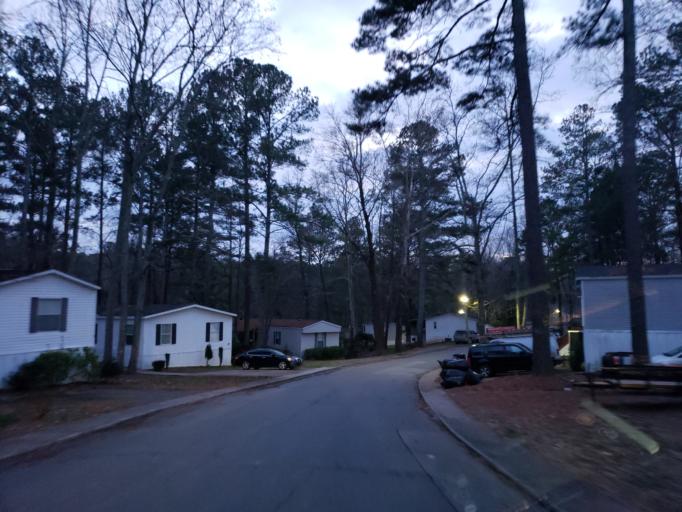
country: US
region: Georgia
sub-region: Cobb County
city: Kennesaw
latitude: 34.0217
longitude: -84.6318
